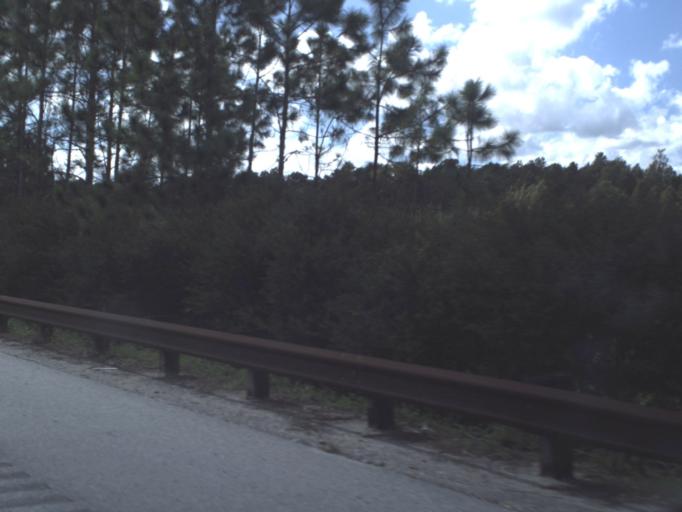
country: US
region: Florida
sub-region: Hillsborough County
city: Greater Northdale
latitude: 28.1277
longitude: -82.5482
